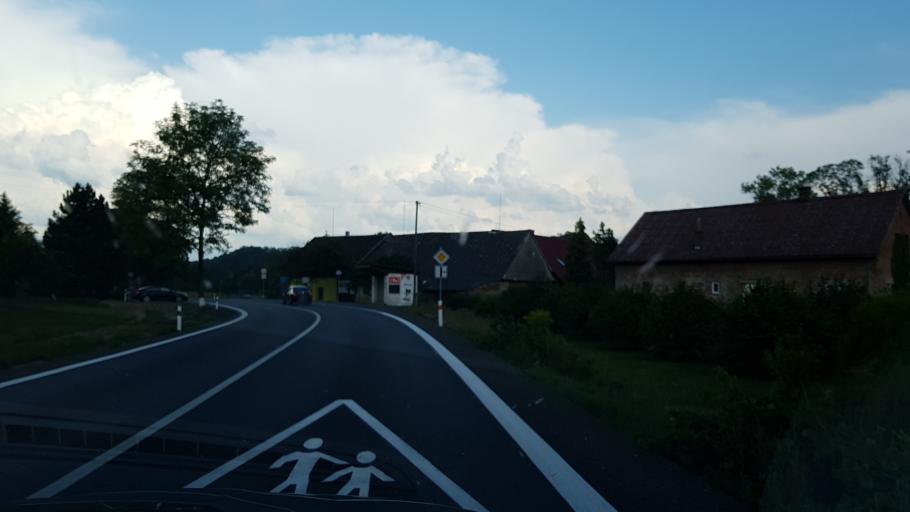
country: CZ
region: Pardubicky
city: Zamberk
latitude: 50.0924
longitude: 16.4300
